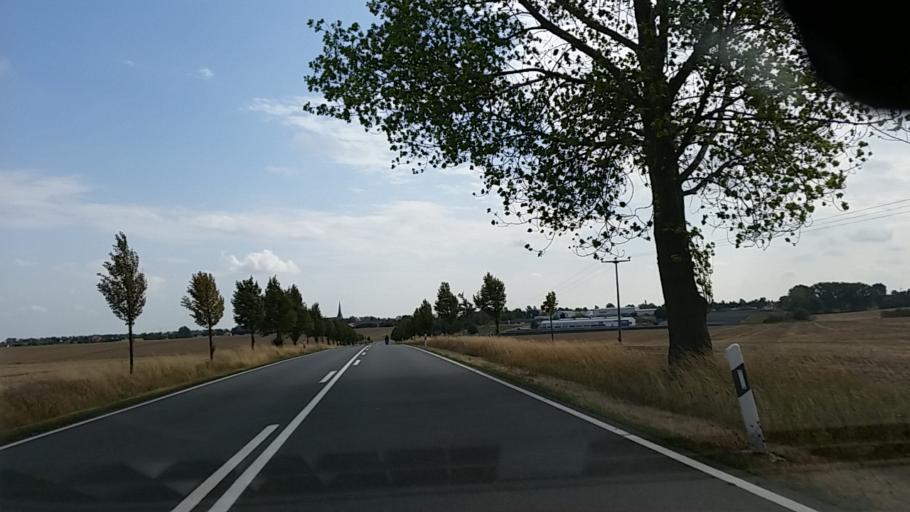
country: DE
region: Saxony-Anhalt
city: Nemsdorf-Gohrendorf
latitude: 51.3536
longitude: 11.6313
